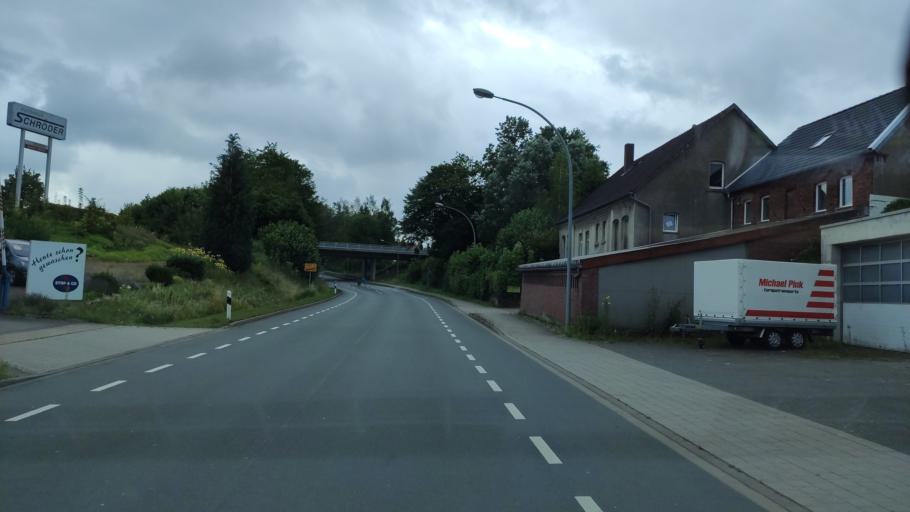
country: DE
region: North Rhine-Westphalia
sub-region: Regierungsbezirk Detmold
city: Steinheim
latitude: 51.8648
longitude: 9.1046
